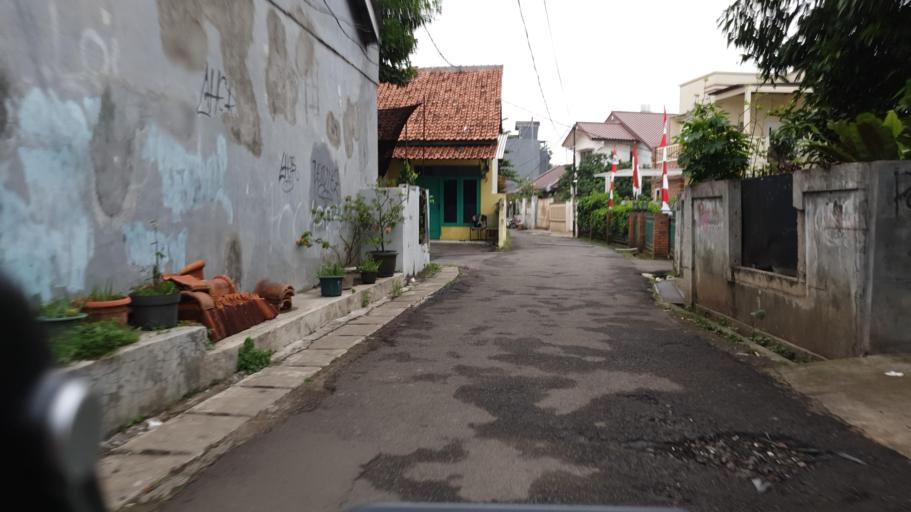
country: ID
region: West Java
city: Pamulang
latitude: -6.3288
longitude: 106.7722
